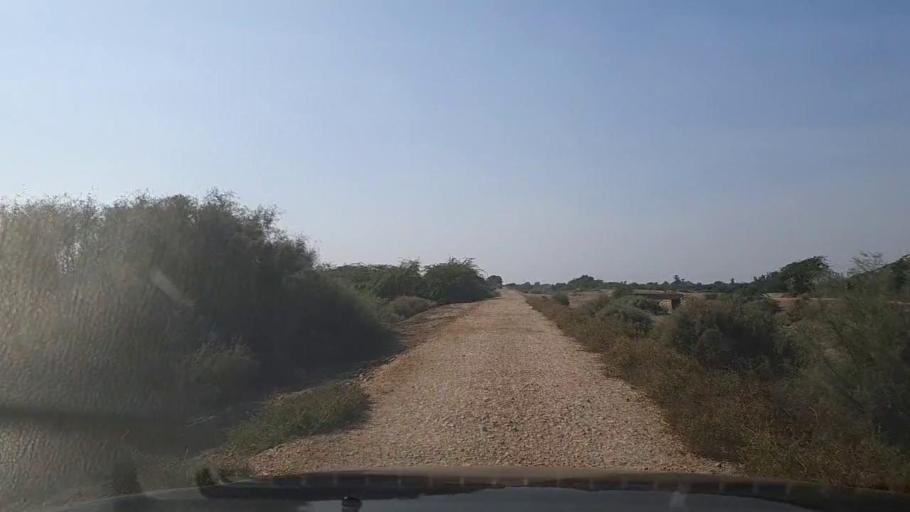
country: PK
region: Sindh
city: Gharo
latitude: 24.7114
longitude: 67.7463
